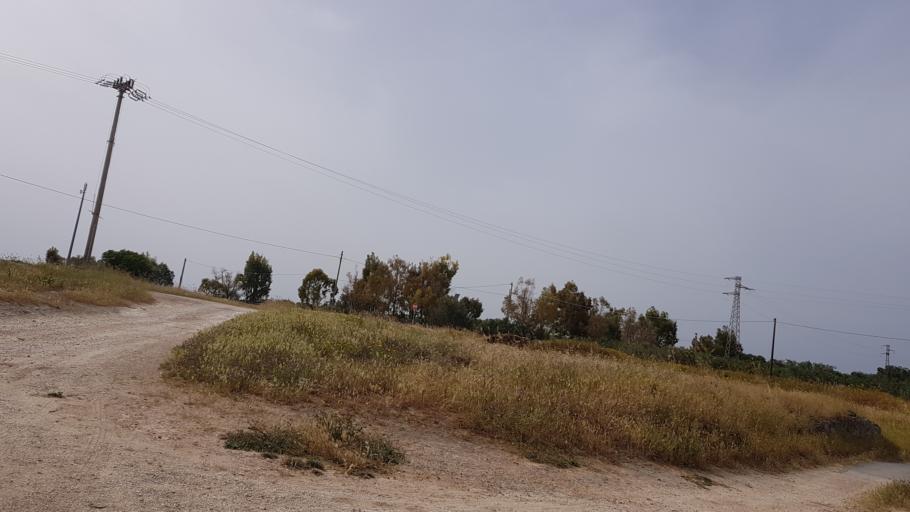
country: IT
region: Apulia
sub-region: Provincia di Brindisi
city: San Vito dei Normanni
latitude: 40.6647
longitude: 17.7941
